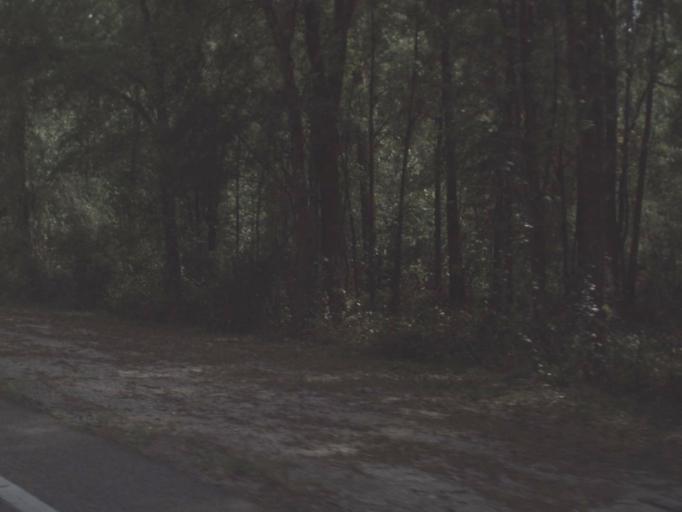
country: US
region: Florida
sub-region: Pasco County
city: Lacoochee
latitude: 28.4743
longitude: -82.0547
